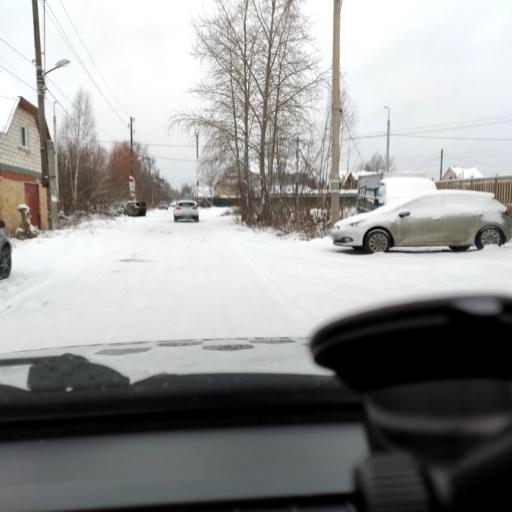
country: RU
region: Perm
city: Perm
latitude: 58.0568
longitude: 56.3616
